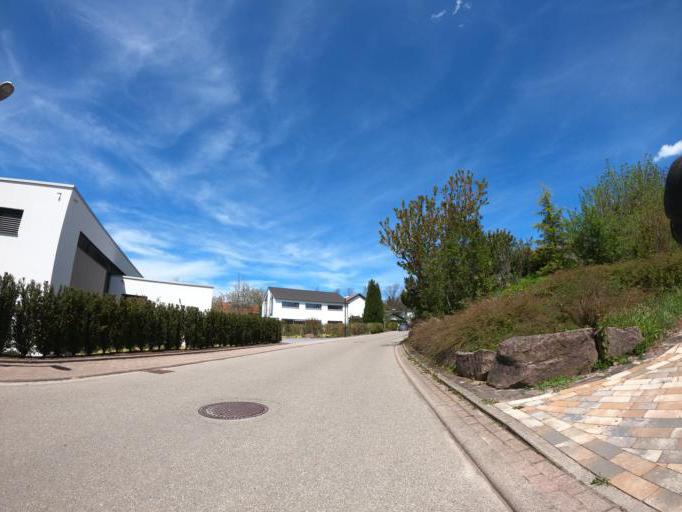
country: DE
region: Baden-Wuerttemberg
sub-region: Karlsruhe Region
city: Engelsbrand
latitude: 48.8347
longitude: 8.6461
